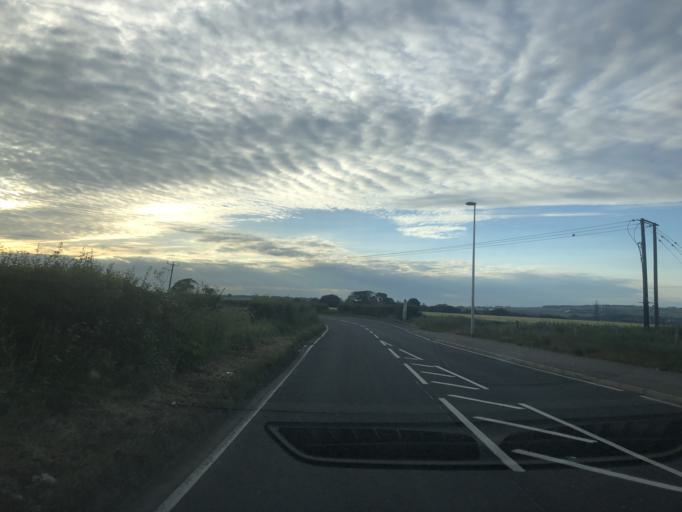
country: GB
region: Scotland
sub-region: Fife
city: Buckhaven
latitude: 56.1786
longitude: -3.0490
